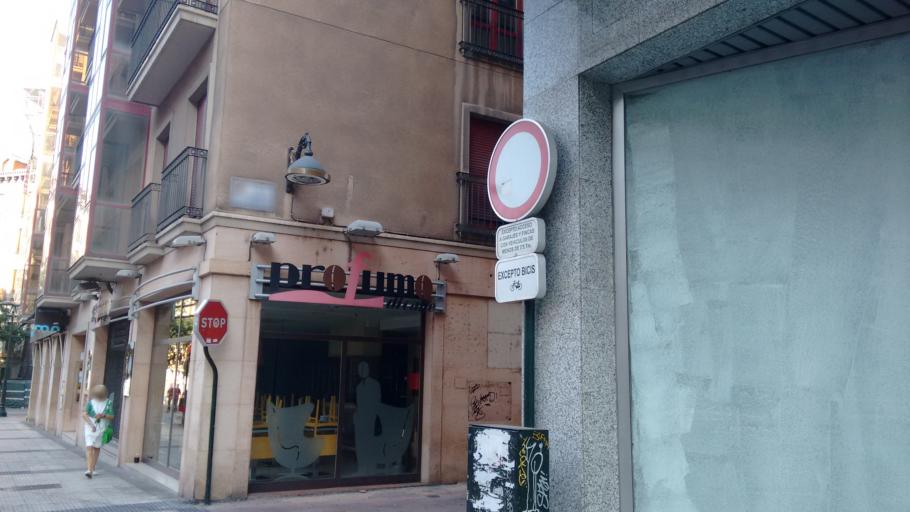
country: ES
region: Aragon
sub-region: Provincia de Zaragoza
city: Zaragoza
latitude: 41.6536
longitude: -0.8841
